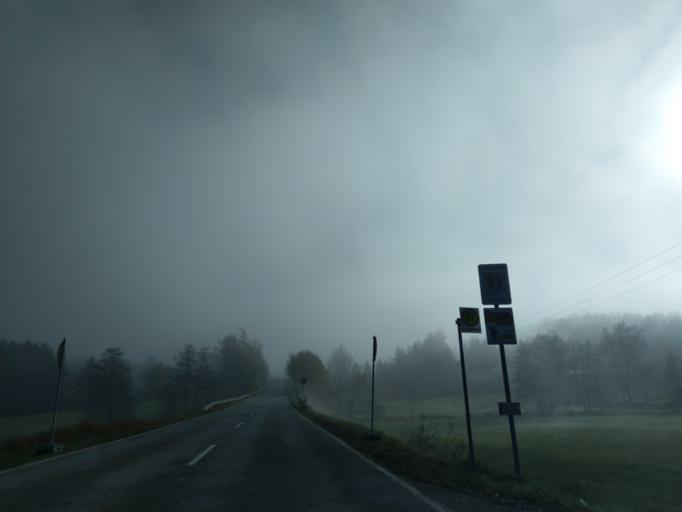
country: DE
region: Bavaria
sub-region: Lower Bavaria
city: Aussernzell
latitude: 48.7210
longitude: 13.2485
